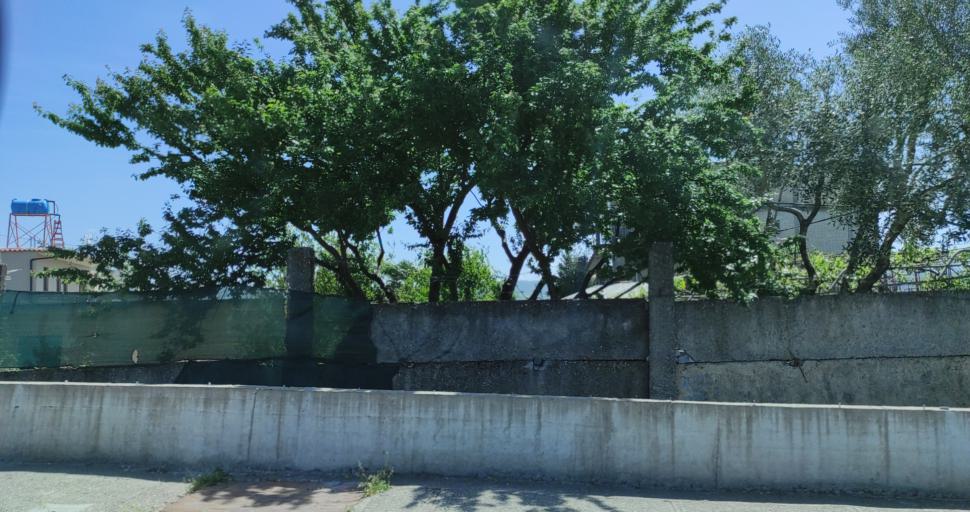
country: AL
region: Shkoder
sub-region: Rrethi i Shkodres
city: Shkoder
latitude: 42.0917
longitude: 19.5346
